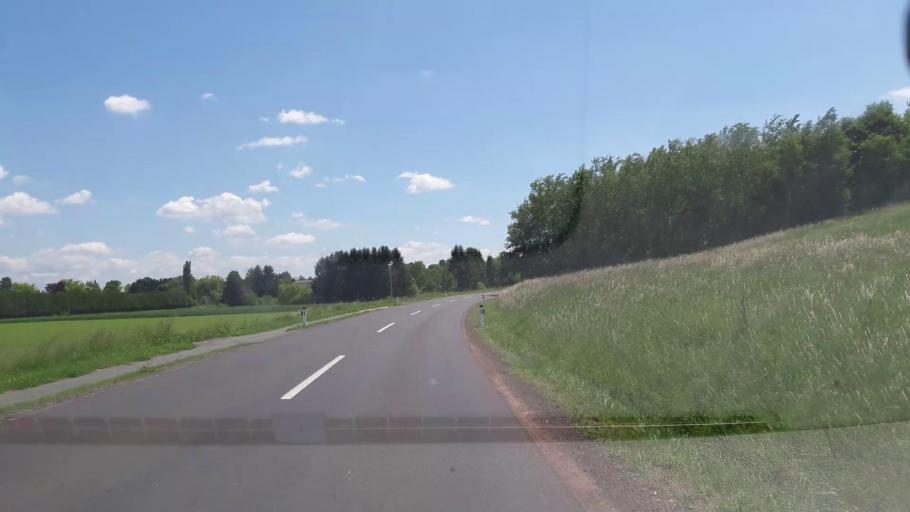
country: AT
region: Burgenland
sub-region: Politischer Bezirk Jennersdorf
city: Jennersdorf
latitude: 46.9427
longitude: 16.1306
